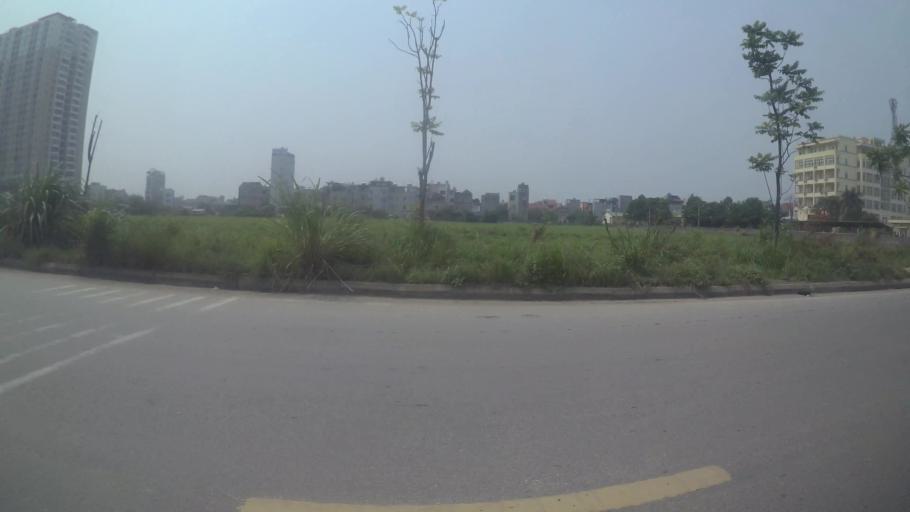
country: VN
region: Ha Noi
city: Cau Dien
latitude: 21.0104
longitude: 105.7190
